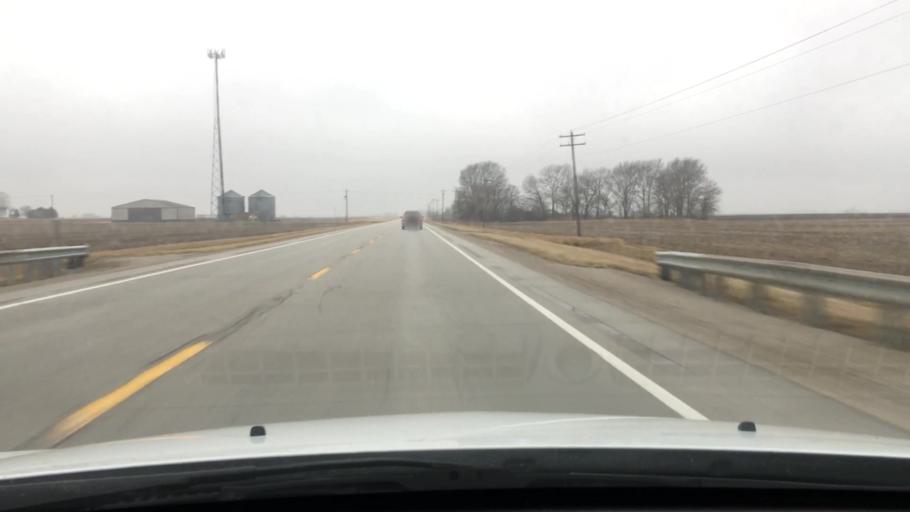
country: US
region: Illinois
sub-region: Livingston County
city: Flanagan
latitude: 40.8718
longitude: -88.8072
